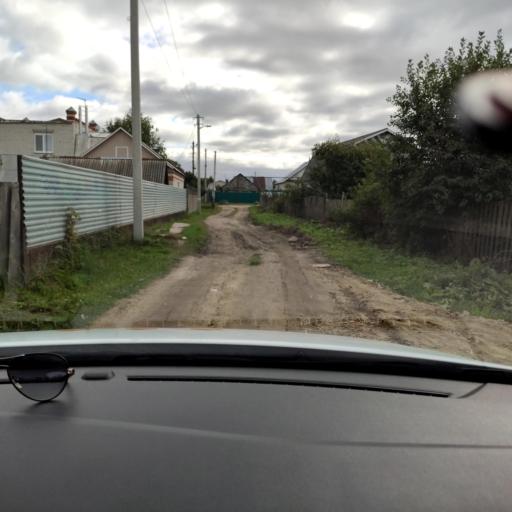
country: RU
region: Tatarstan
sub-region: Gorod Kazan'
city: Kazan
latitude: 55.7219
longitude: 49.1039
